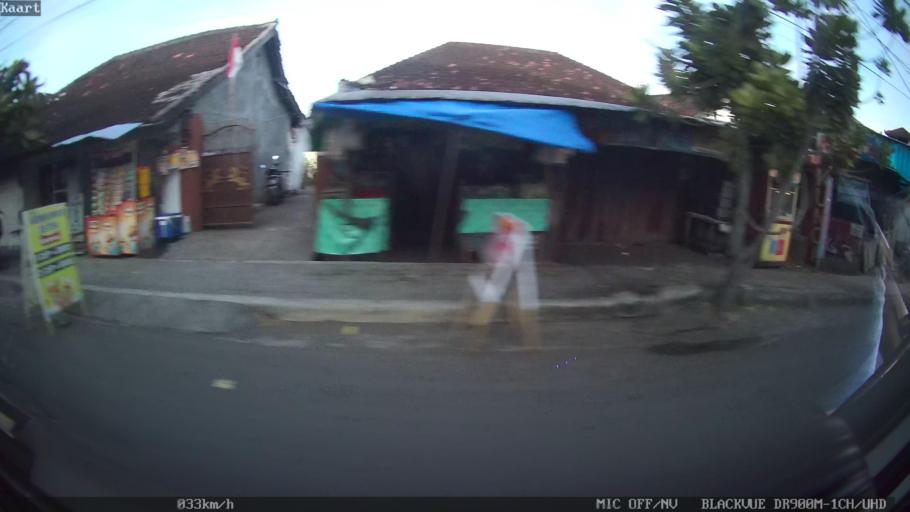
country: ID
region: Bali
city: Banjar Kertasari
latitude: -8.6227
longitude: 115.2097
